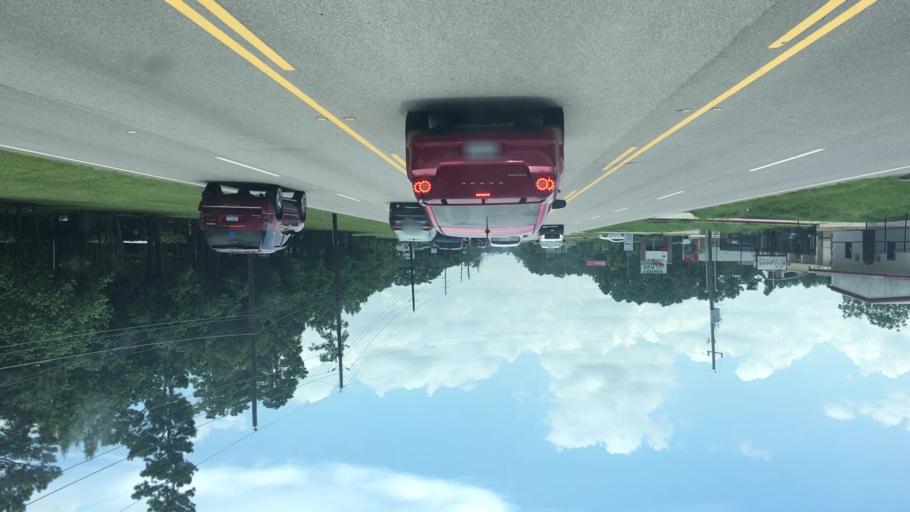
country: US
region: Texas
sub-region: Harris County
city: Atascocita
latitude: 29.9879
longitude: -95.1945
